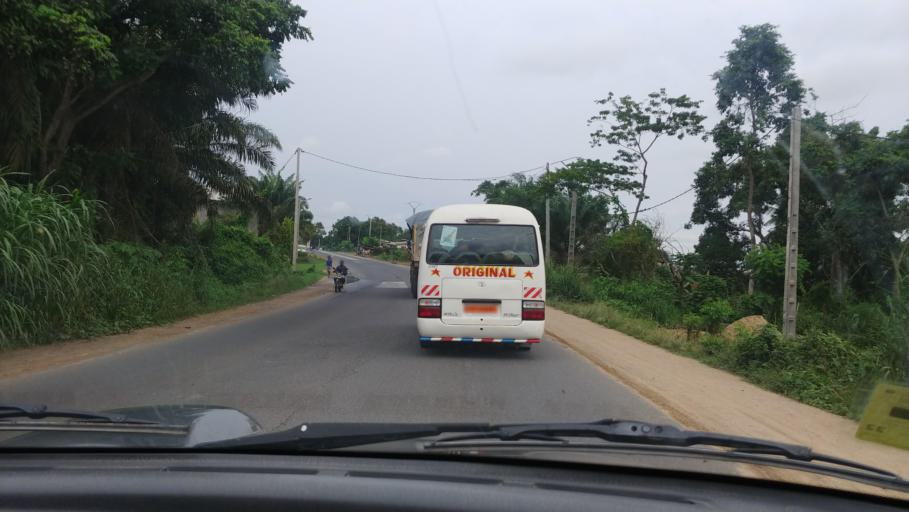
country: CM
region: Littoral
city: Dibombari
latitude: 4.1508
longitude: 9.5874
